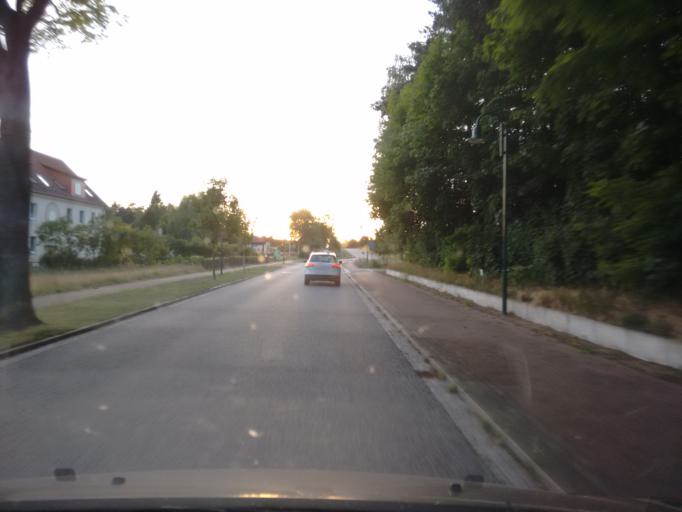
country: DE
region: Brandenburg
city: Mixdorf
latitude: 52.1602
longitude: 14.3869
